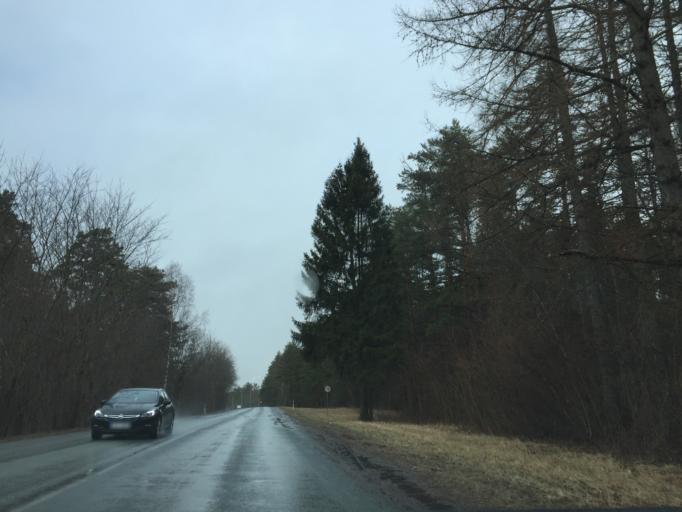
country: EE
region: Laeaene
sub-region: Haapsalu linn
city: Haapsalu
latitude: 58.9173
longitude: 23.5498
